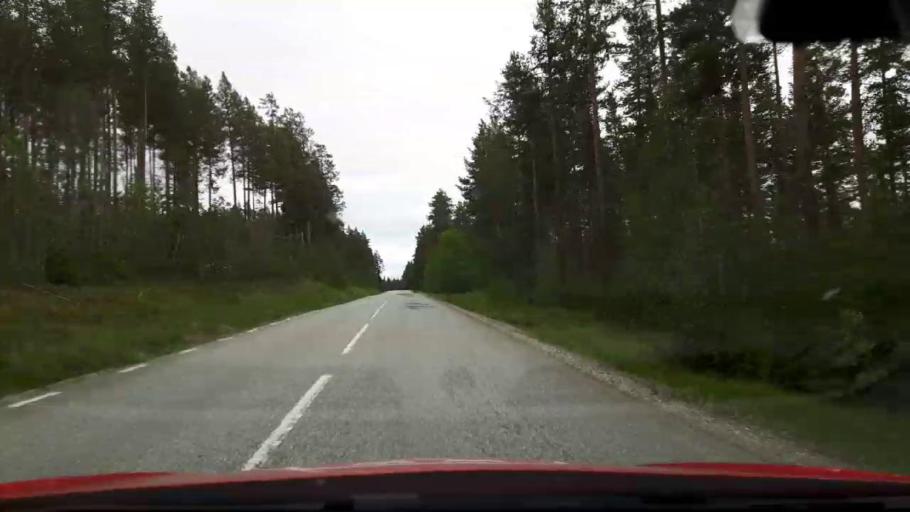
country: SE
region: Jaemtland
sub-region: Ragunda Kommun
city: Hammarstrand
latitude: 63.2483
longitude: 15.9095
